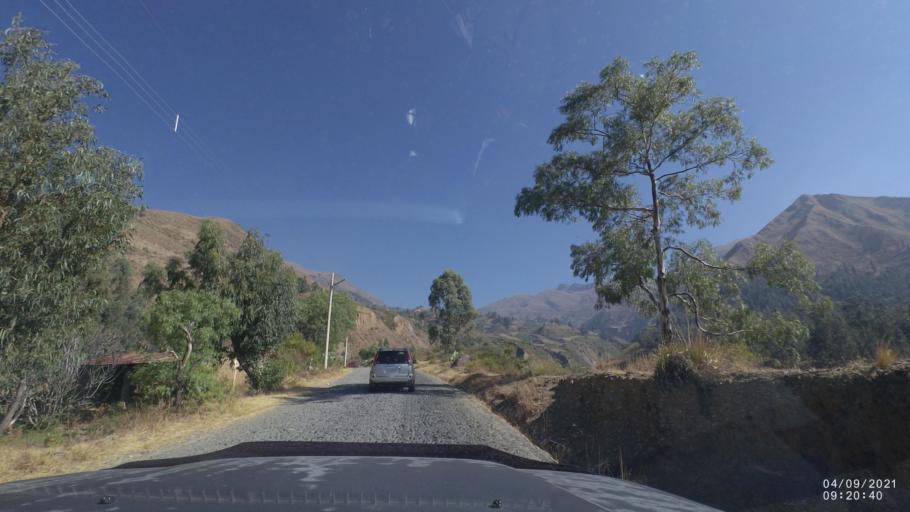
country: BO
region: Cochabamba
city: Sipe Sipe
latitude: -17.3627
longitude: -66.3636
